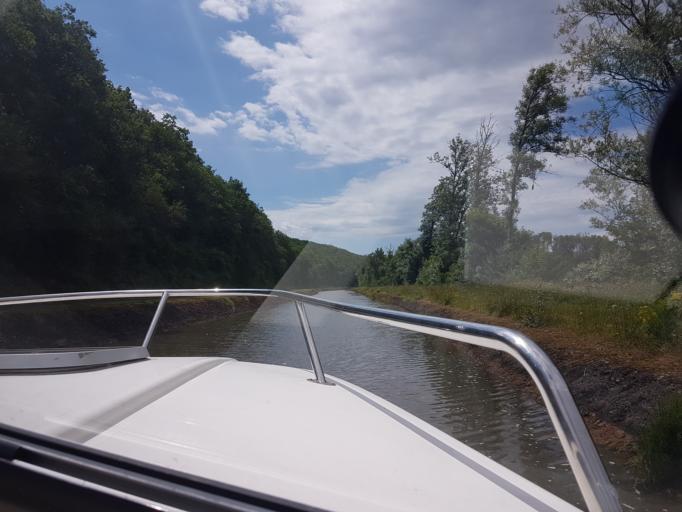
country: FR
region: Bourgogne
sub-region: Departement de la Nievre
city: Clamecy
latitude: 47.5074
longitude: 3.5207
